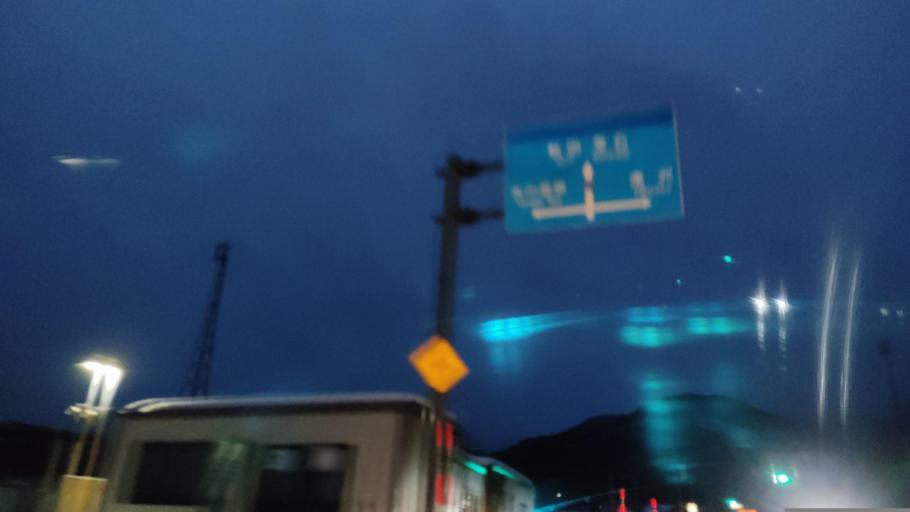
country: JP
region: Iwate
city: Morioka-shi
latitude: 39.6343
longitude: 141.0933
